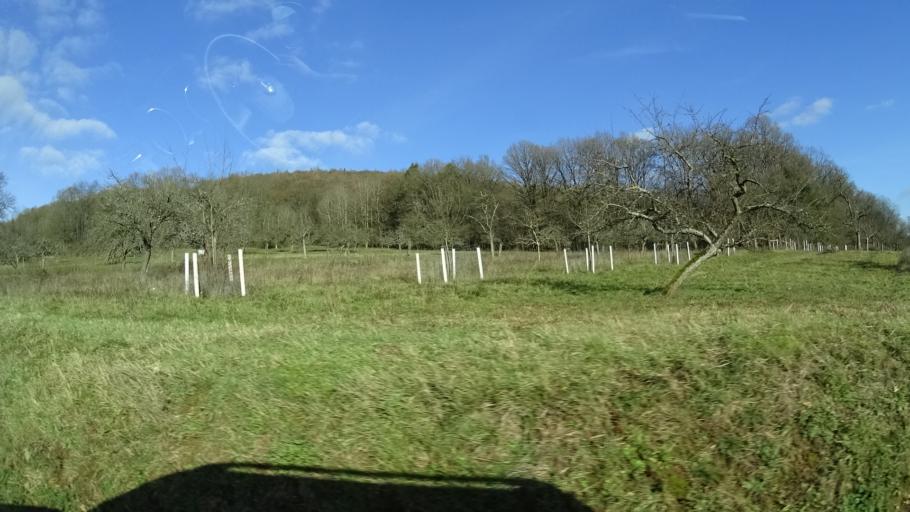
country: DE
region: Baden-Wuerttemberg
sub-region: Regierungsbezirk Stuttgart
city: Freudenberg
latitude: 49.7786
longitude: 9.3229
